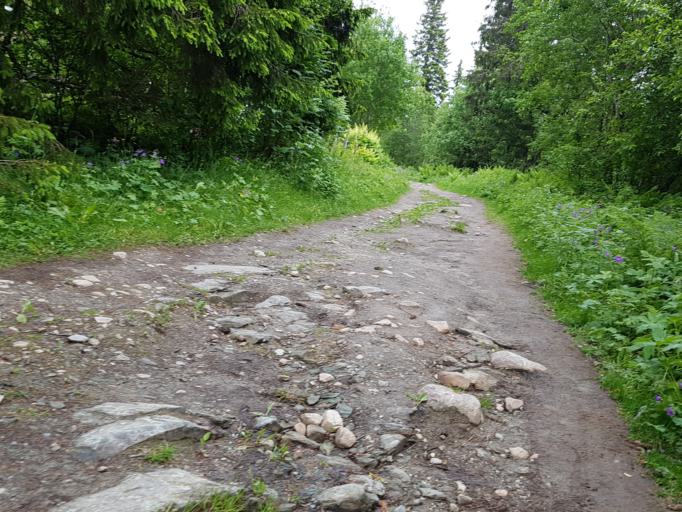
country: NO
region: Sor-Trondelag
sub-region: Trondheim
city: Trondheim
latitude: 63.3994
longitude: 10.2941
